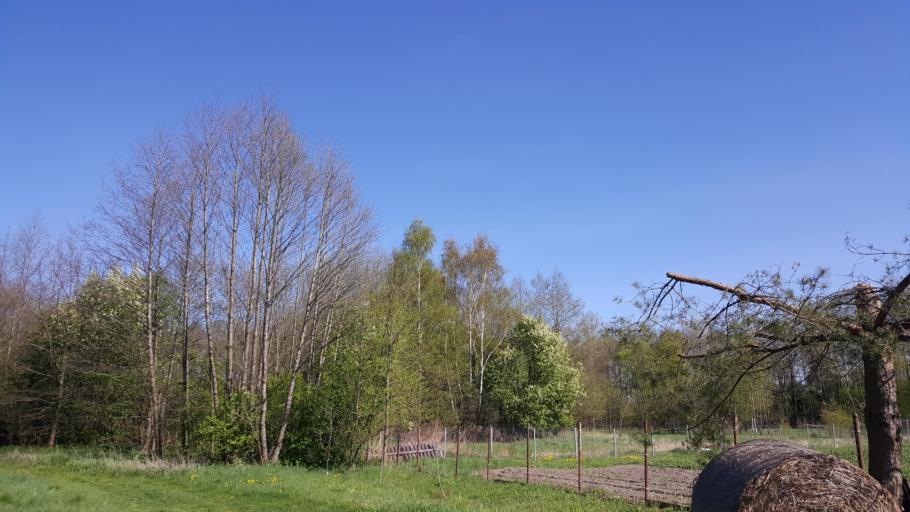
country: BY
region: Brest
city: Kamyanyets
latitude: 52.4349
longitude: 23.8745
